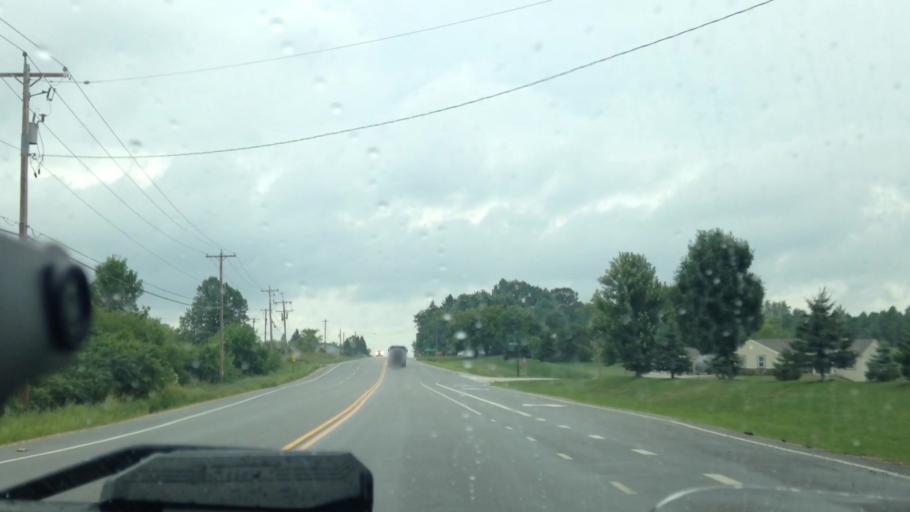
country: US
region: Wisconsin
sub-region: Washington County
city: Richfield
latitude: 43.2249
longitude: -88.1782
